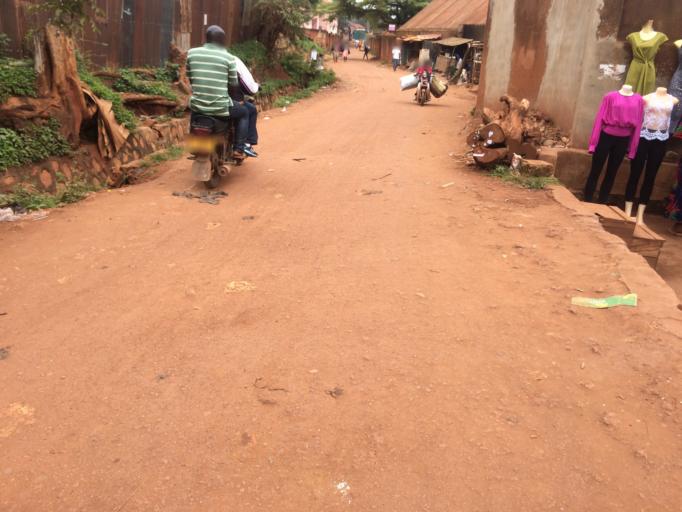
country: UG
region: Central Region
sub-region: Kampala District
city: Kampala
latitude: 0.2916
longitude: 32.6038
